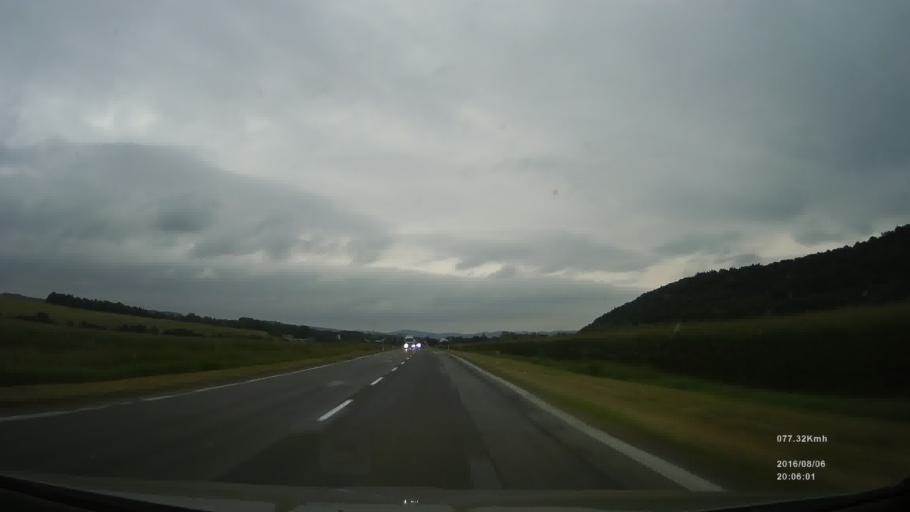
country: SK
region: Presovsky
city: Stropkov
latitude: 49.2302
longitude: 21.6296
